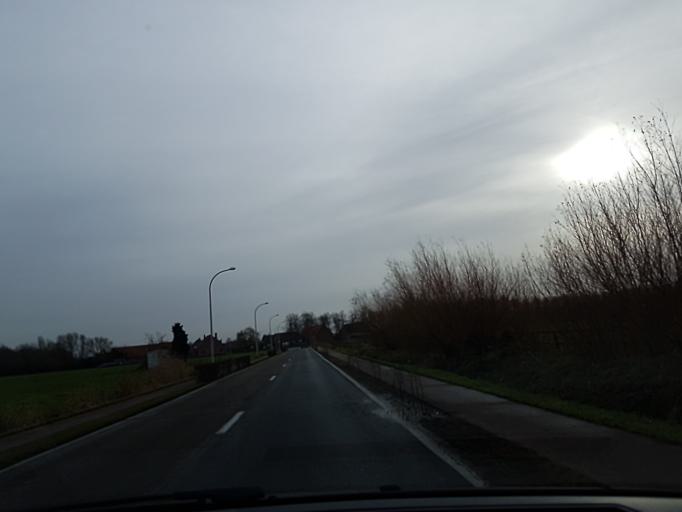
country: BE
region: Flanders
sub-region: Provincie Antwerpen
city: Lier
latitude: 51.1056
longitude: 4.5991
